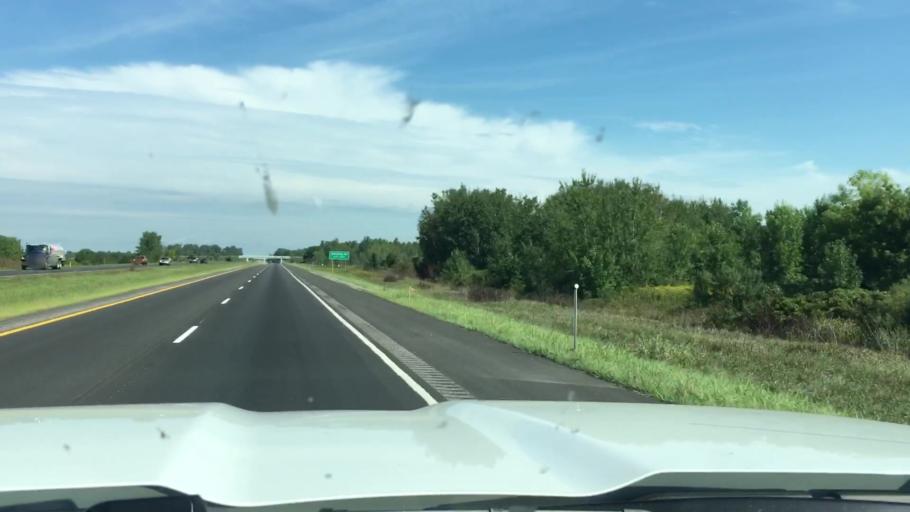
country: US
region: Michigan
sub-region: Saginaw County
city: Freeland
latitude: 43.5589
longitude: -84.1388
